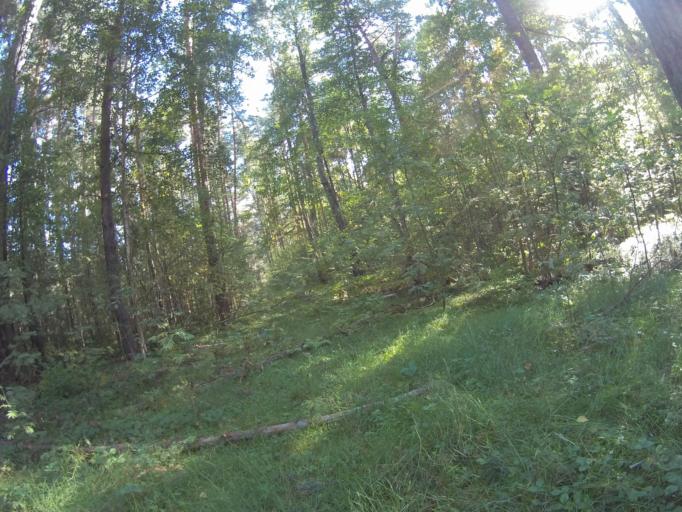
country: RU
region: Vladimir
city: Kommunar
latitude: 56.0740
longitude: 40.4457
